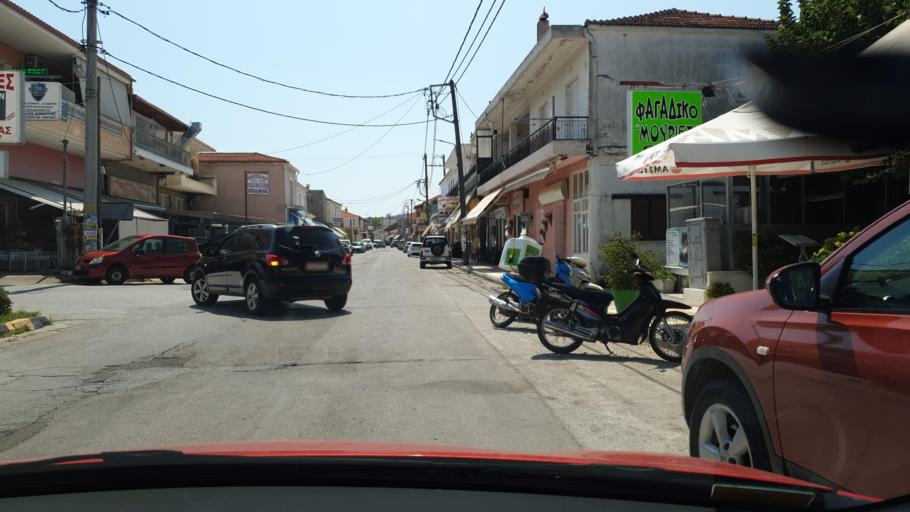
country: GR
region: Central Greece
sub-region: Nomos Evvoias
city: Oxilithos
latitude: 38.5009
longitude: 24.1104
